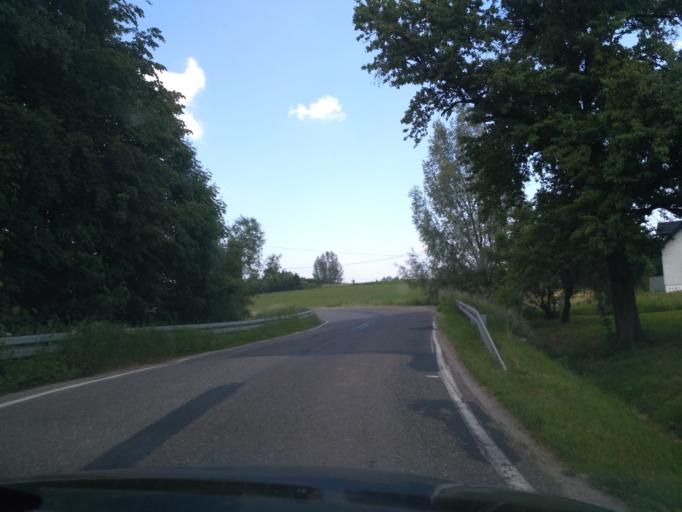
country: PL
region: Subcarpathian Voivodeship
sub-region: Powiat lancucki
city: Handzlowka
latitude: 49.9707
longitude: 22.1912
